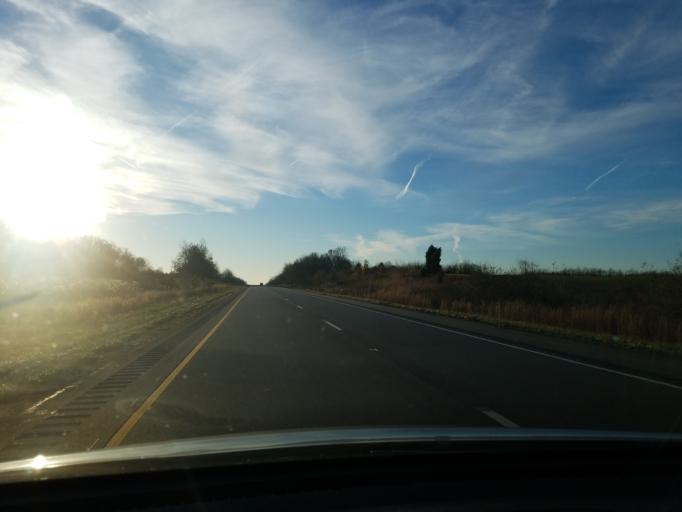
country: US
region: Indiana
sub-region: Spencer County
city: Dale
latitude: 38.1993
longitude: -87.1227
